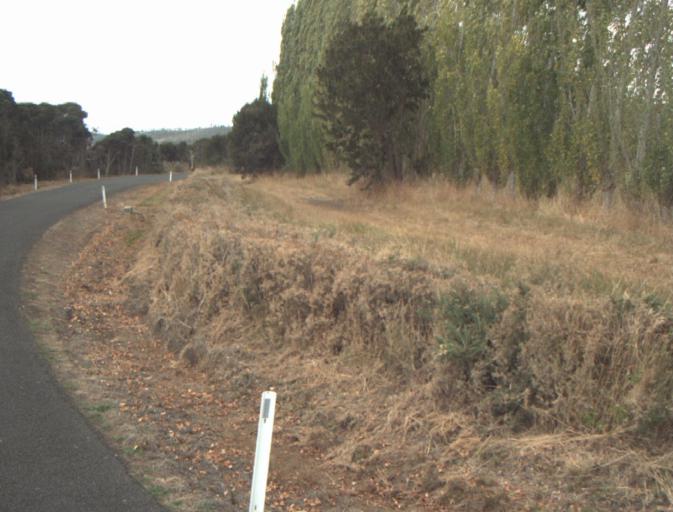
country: AU
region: Tasmania
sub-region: Launceston
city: Mayfield
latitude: -41.2902
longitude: 146.9906
